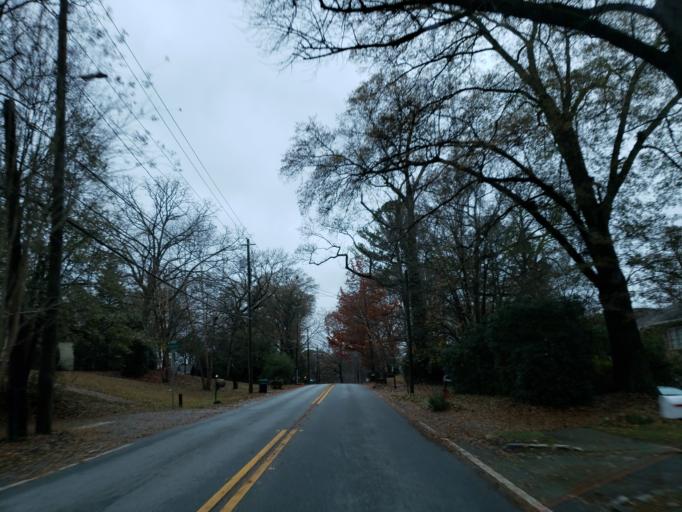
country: US
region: Georgia
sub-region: DeKalb County
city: Druid Hills
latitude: 33.7937
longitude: -84.3362
